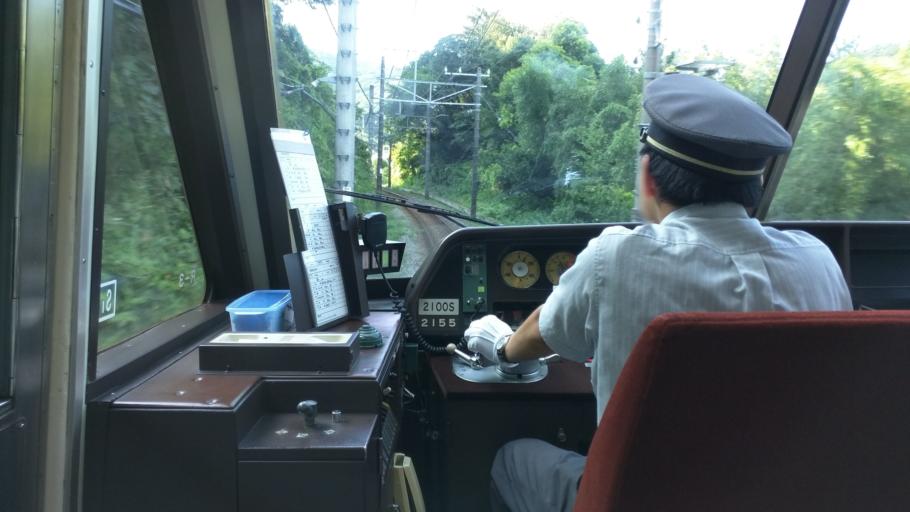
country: JP
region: Shizuoka
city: Atami
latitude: 35.0615
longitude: 139.0674
